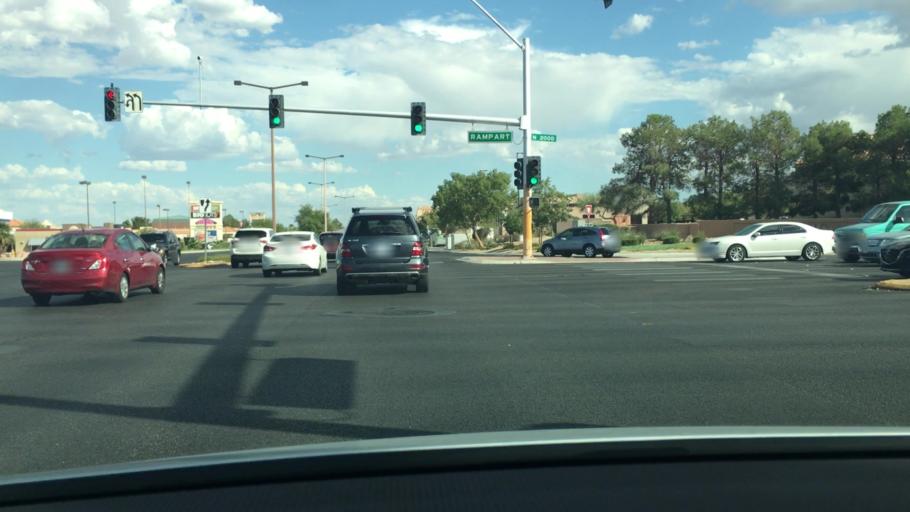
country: US
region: Nevada
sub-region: Clark County
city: Summerlin South
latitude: 36.1998
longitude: -115.2827
